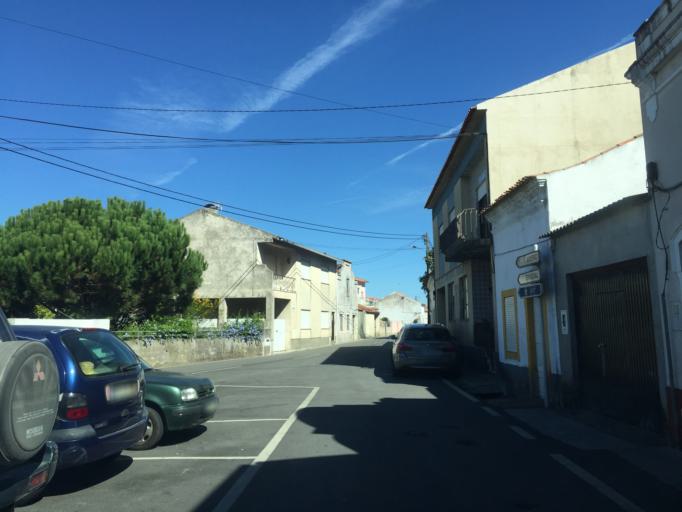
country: PT
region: Coimbra
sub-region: Figueira da Foz
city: Tavarede
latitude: 40.2140
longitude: -8.8480
